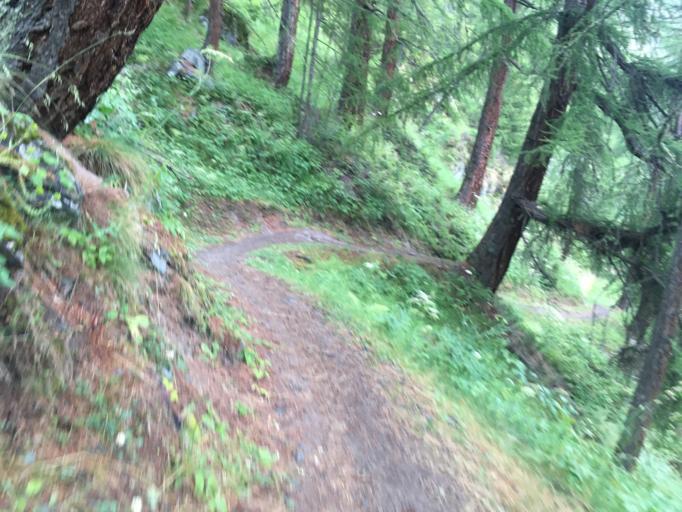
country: CH
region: Valais
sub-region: Visp District
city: Zermatt
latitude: 46.0104
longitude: 7.7307
